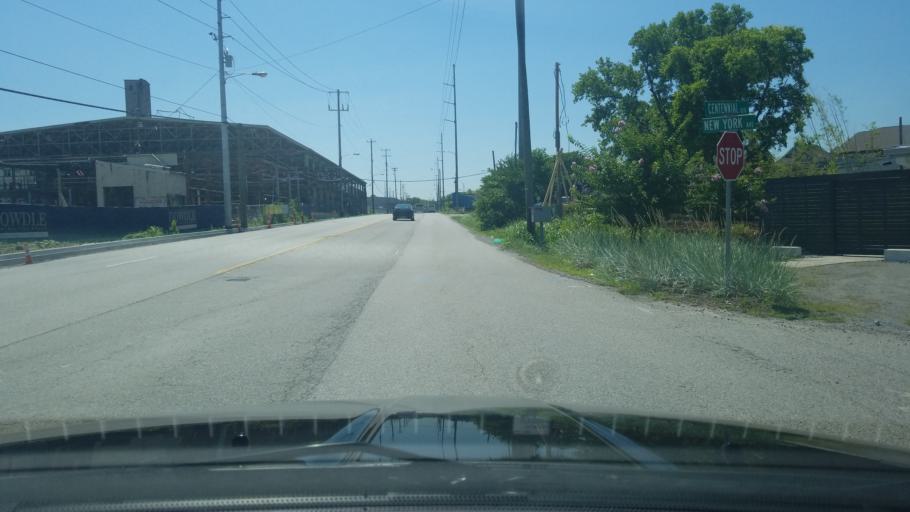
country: US
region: Tennessee
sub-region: Davidson County
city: Belle Meade
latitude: 36.1653
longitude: -86.8543
